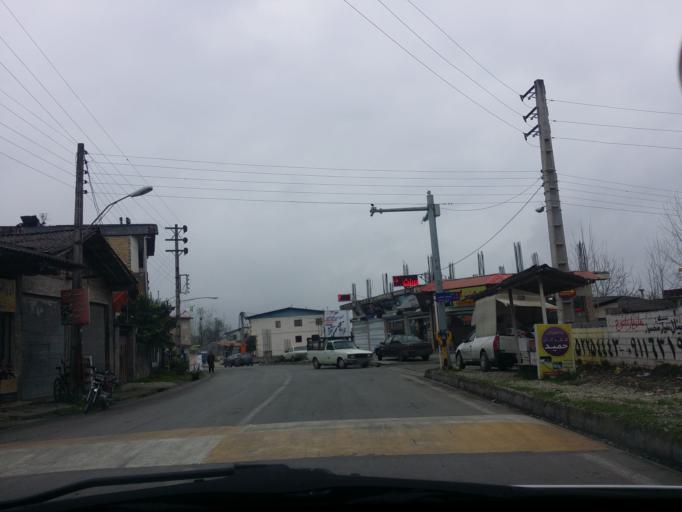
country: IR
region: Mazandaran
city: Chalus
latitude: 36.6630
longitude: 51.3950
